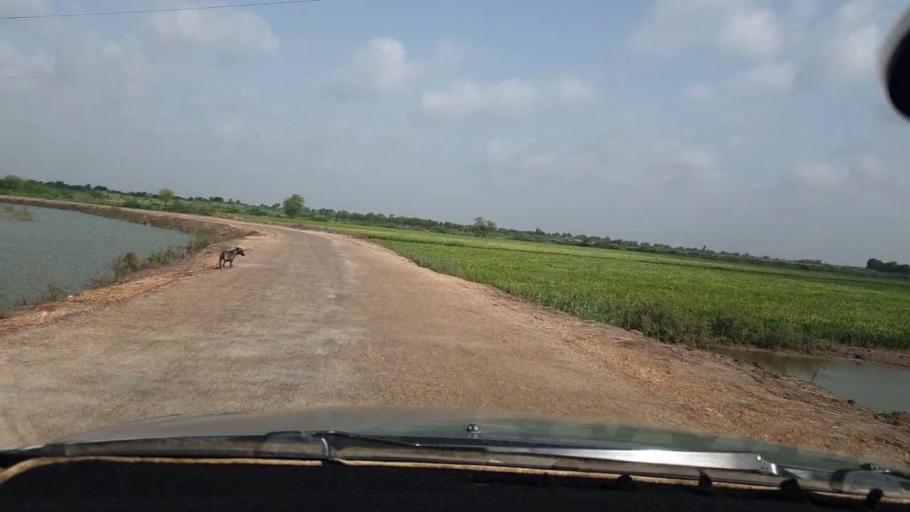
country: PK
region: Sindh
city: Tando Bago
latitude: 24.7752
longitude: 68.9851
